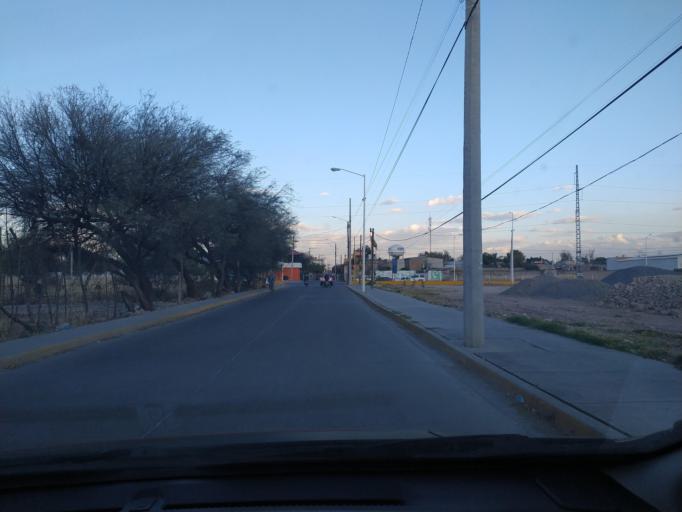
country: LA
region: Oudomxai
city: Muang La
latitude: 21.0138
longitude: 101.8706
